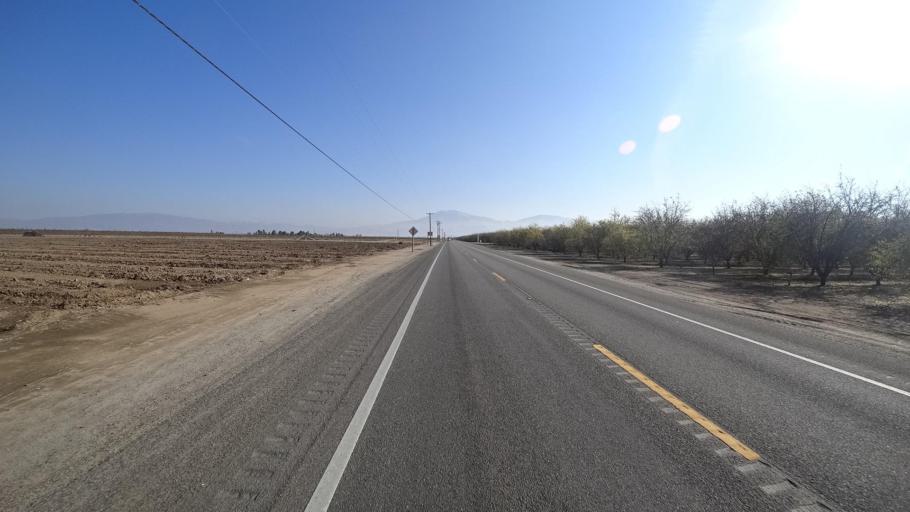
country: US
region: California
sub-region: Kern County
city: Weedpatch
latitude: 35.2088
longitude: -118.9070
